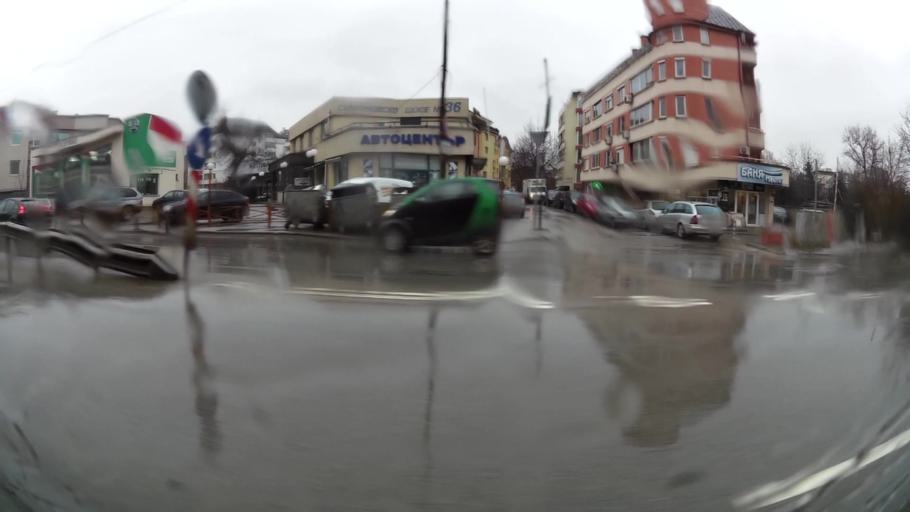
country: BG
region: Sofia-Capital
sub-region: Stolichna Obshtina
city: Sofia
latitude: 42.6532
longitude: 23.3359
